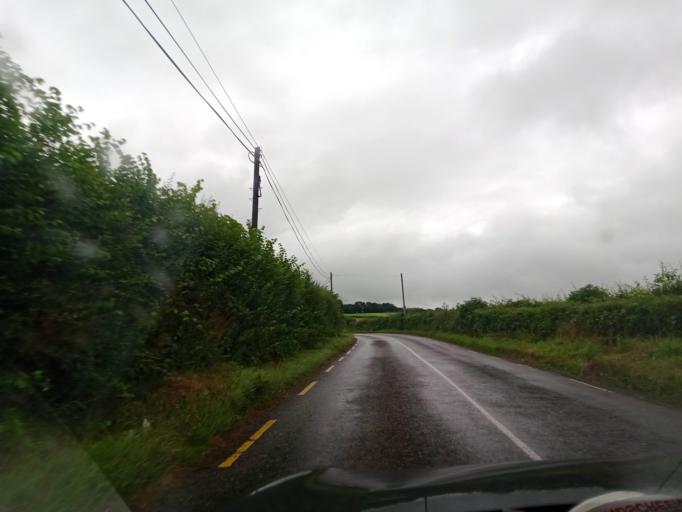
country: IE
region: Leinster
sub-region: Laois
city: Abbeyleix
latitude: 52.9107
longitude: -7.3154
